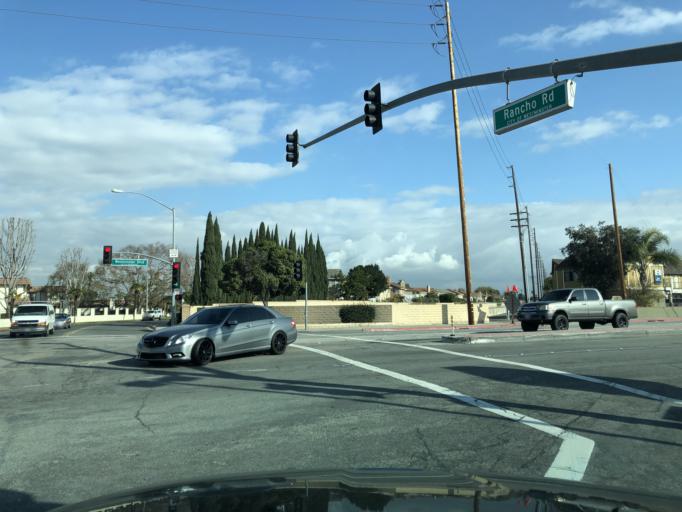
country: US
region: California
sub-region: Orange County
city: Westminster
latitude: 33.7588
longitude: -118.0300
